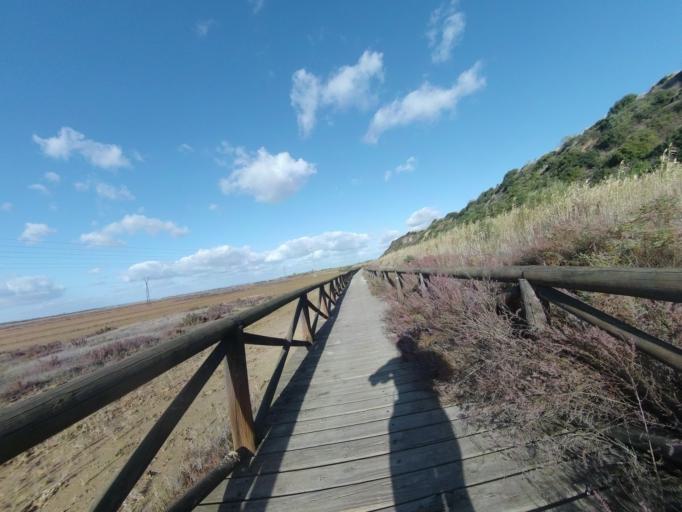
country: ES
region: Andalusia
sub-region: Provincia de Huelva
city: Palos de la Frontera
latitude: 37.2503
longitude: -6.8800
